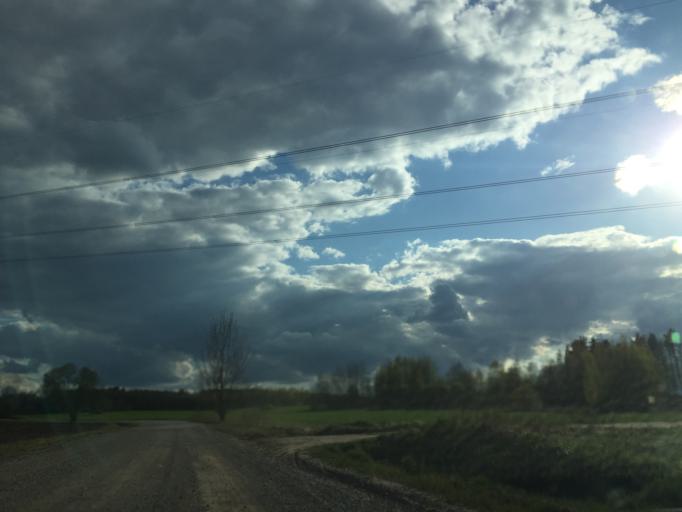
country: LV
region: Beverina
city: Murmuiza
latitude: 57.3917
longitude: 25.4439
